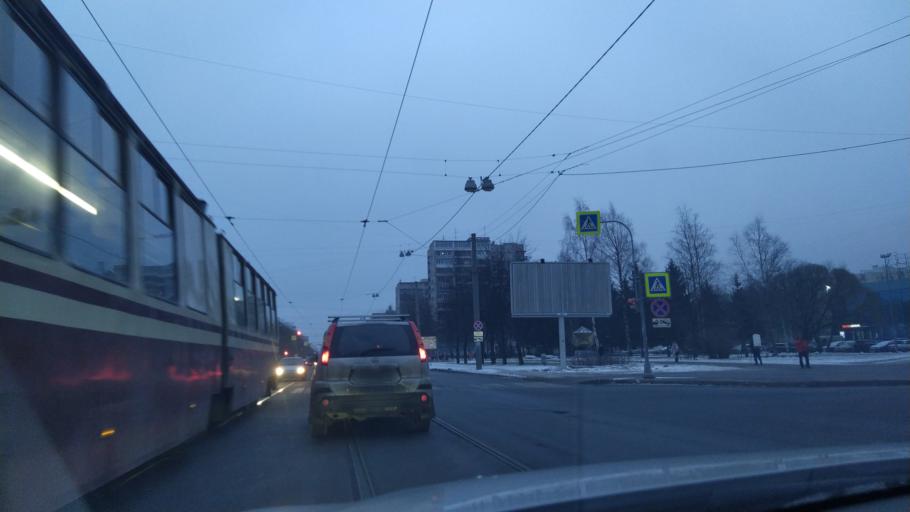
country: RU
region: Leningrad
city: Akademicheskoe
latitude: 60.0111
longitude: 30.4057
